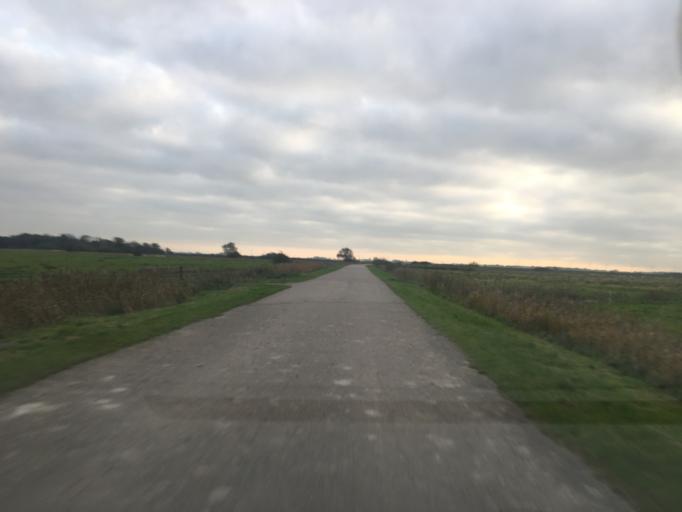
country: DE
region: Schleswig-Holstein
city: Neukirchen
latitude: 54.9132
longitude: 8.7495
